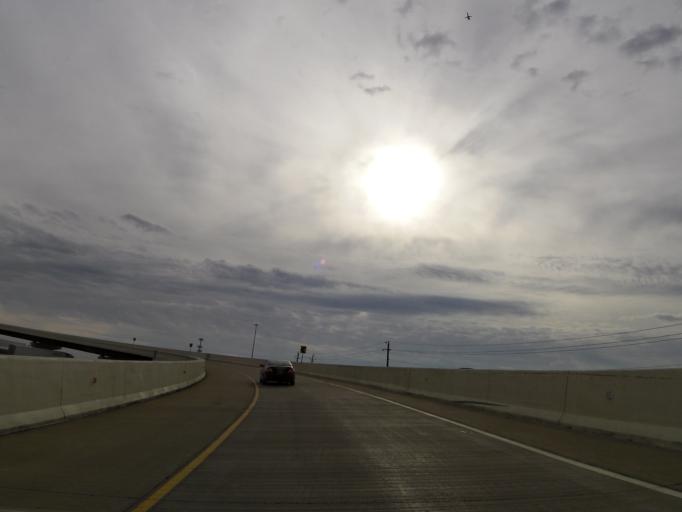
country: US
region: Indiana
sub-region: Marion County
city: Speedway
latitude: 39.8045
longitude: -86.2772
